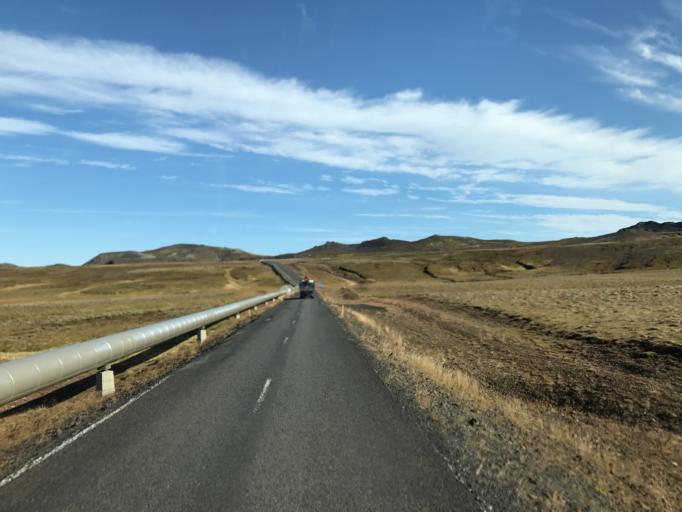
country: IS
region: South
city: Hveragerdi
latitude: 64.1224
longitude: -21.3453
